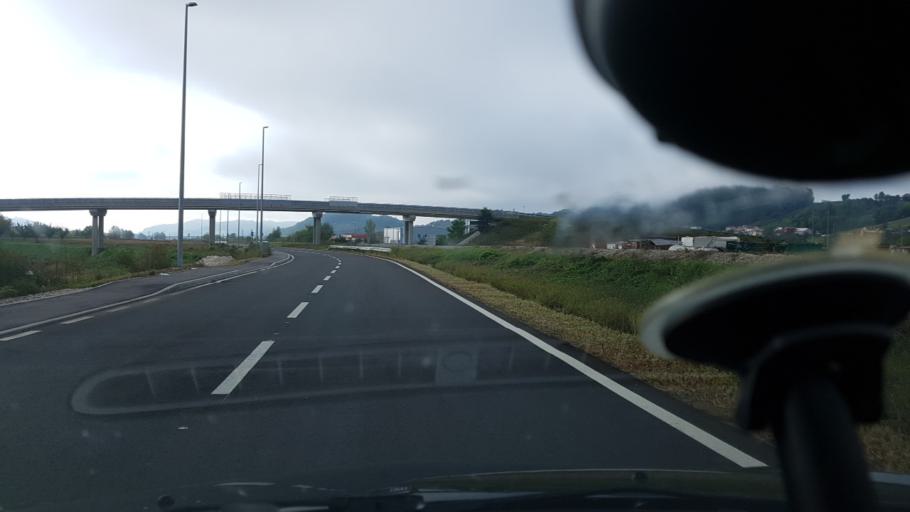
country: HR
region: Krapinsko-Zagorska
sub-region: Grad Krapina
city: Krapina
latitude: 46.1488
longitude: 15.8742
